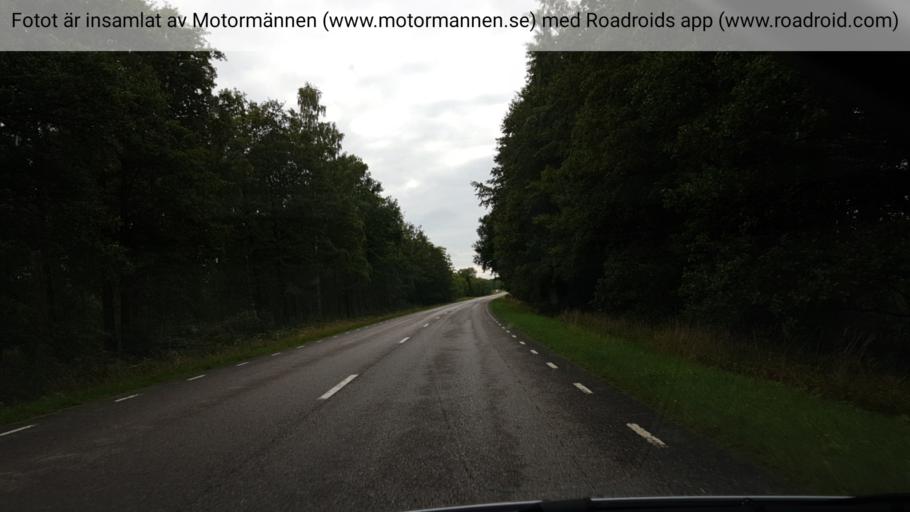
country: SE
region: Vaestra Goetaland
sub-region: Hjo Kommun
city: Hjo
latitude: 58.3216
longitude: 14.2994
